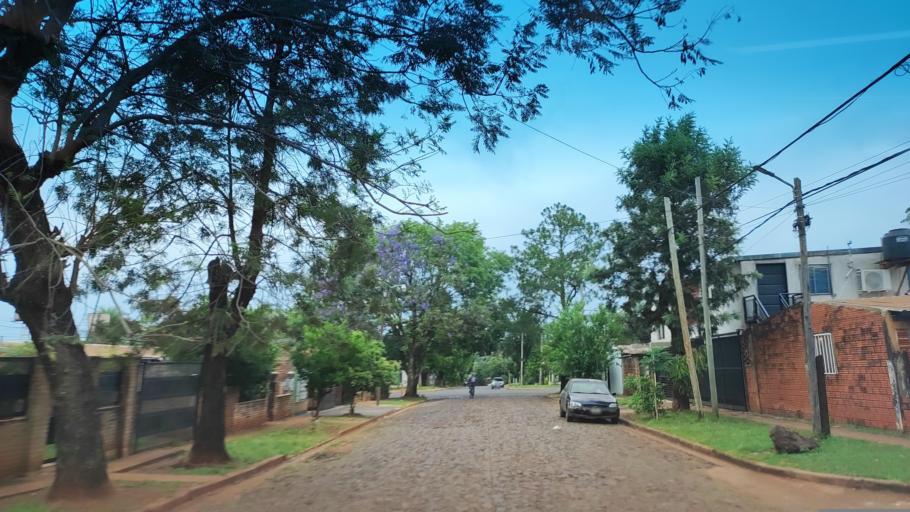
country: AR
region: Misiones
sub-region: Departamento de Capital
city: Posadas
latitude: -27.3806
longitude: -55.9279
